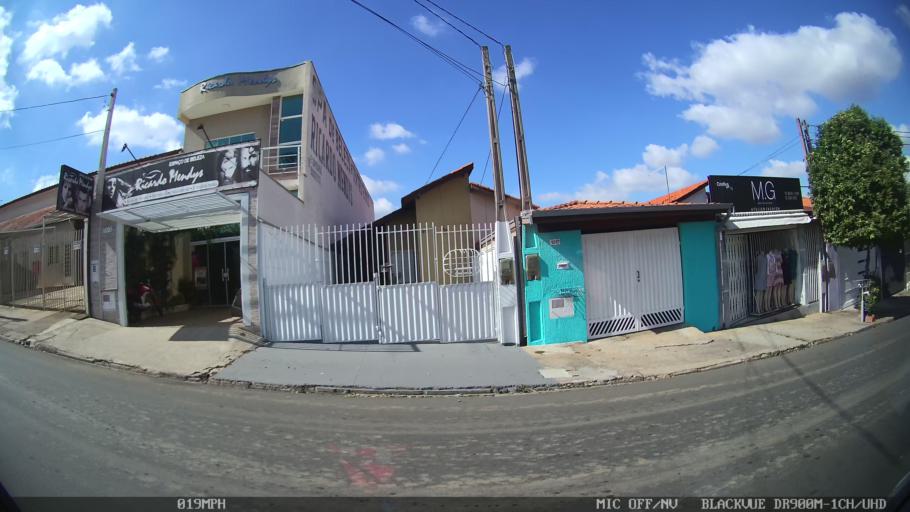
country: BR
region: Sao Paulo
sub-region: Hortolandia
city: Hortolandia
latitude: -22.8851
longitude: -47.2029
